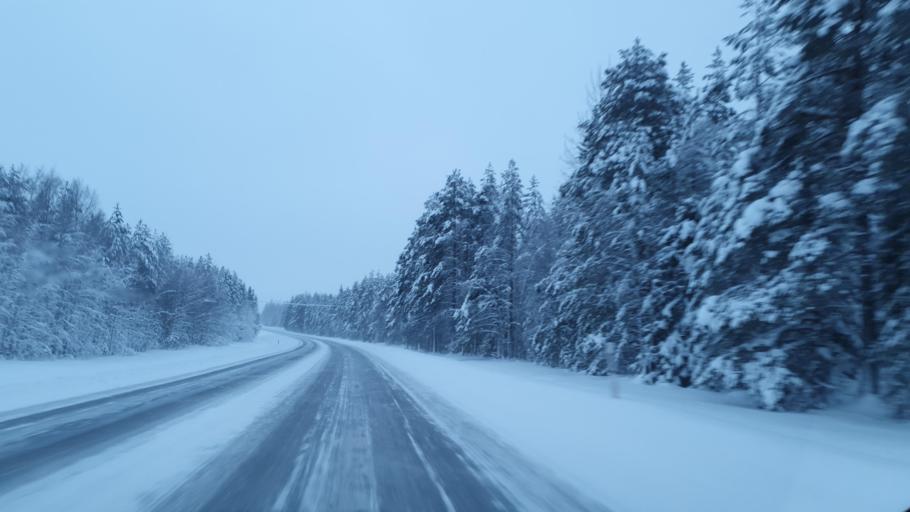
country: FI
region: Kainuu
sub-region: Kajaani
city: Vaala
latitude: 64.5579
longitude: 27.0065
